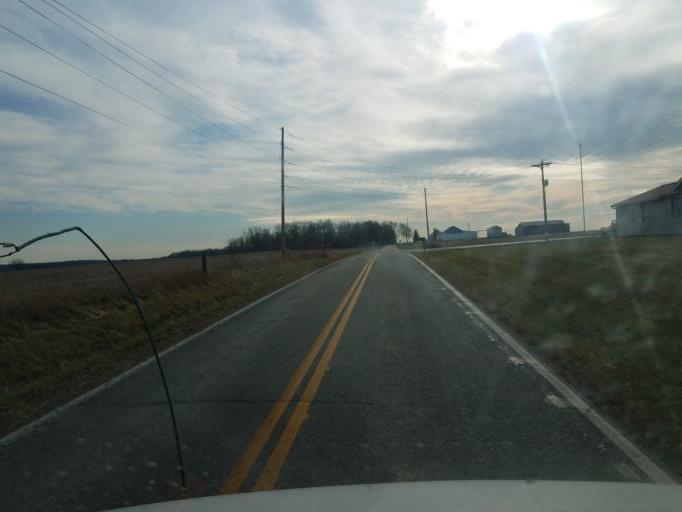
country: US
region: Ohio
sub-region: Delaware County
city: Ashley
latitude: 40.3482
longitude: -82.9660
